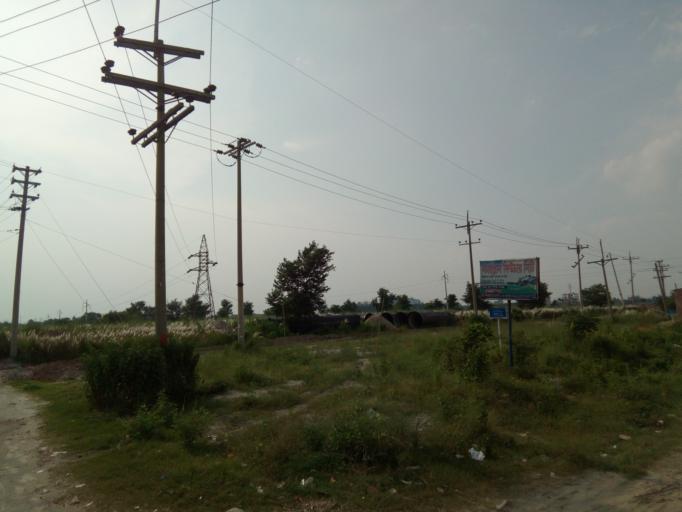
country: BD
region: Dhaka
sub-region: Dhaka
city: Dhaka
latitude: 23.6807
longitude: 90.4034
